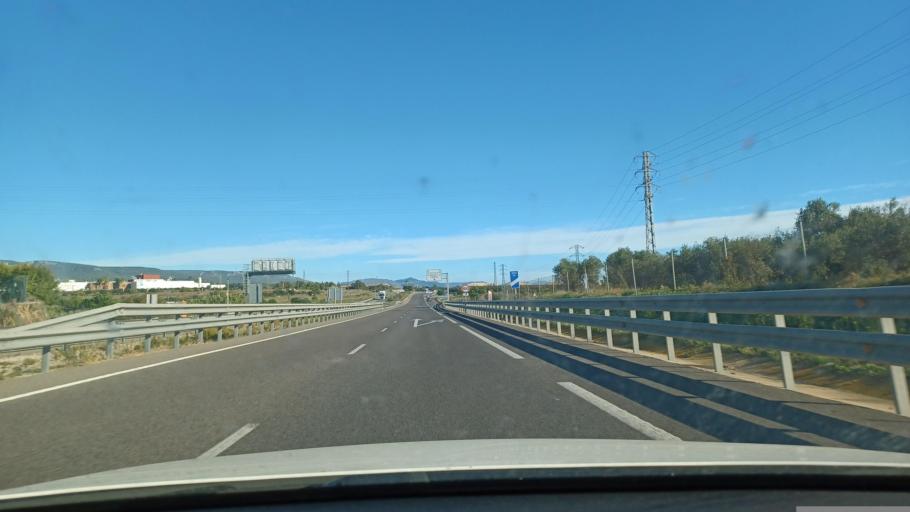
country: ES
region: Catalonia
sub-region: Provincia de Tarragona
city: La Selva
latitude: 41.2181
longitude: 1.1541
